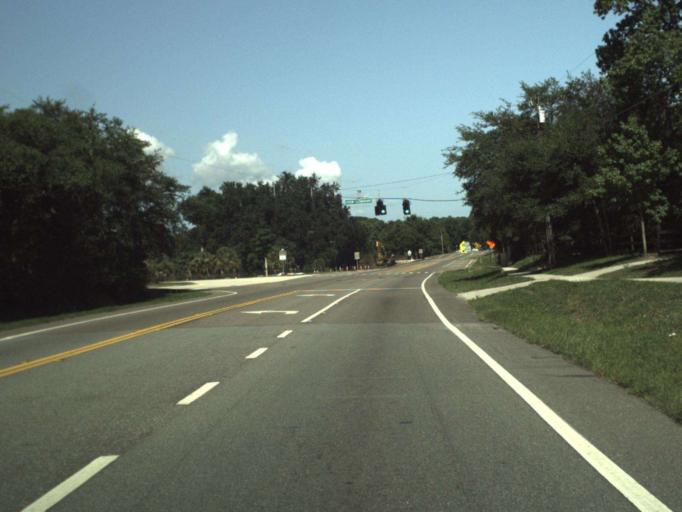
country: US
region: Florida
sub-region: Seminole County
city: Winter Springs
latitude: 28.7045
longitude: -81.2956
